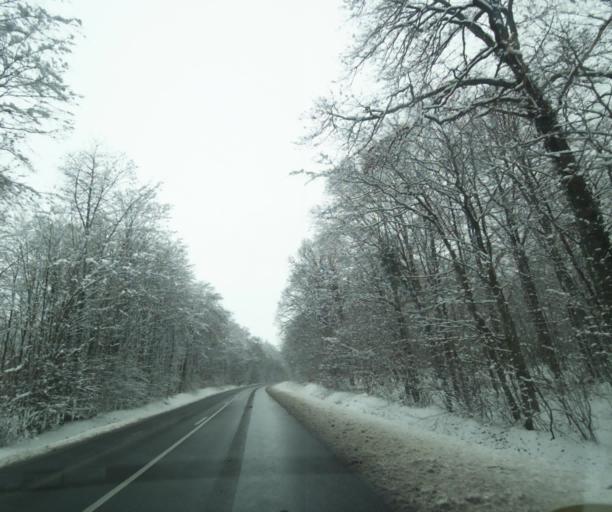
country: FR
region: Champagne-Ardenne
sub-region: Departement de la Haute-Marne
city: Montier-en-Der
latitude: 48.4894
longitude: 4.7767
